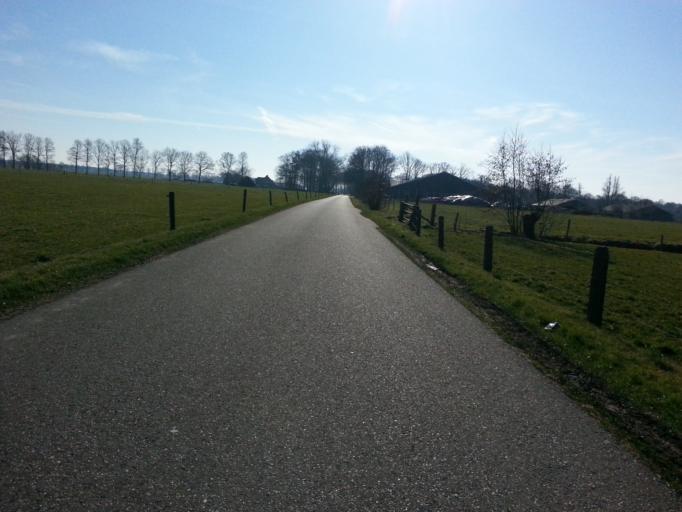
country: NL
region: Utrecht
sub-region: Gemeente Woudenberg
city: Woudenberg
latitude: 52.0698
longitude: 5.4352
